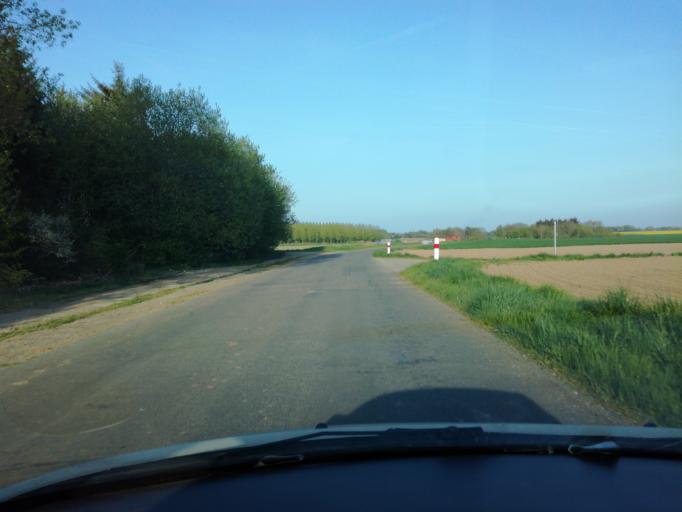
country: FR
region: Picardie
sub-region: Departement de la Somme
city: Poix-de-Picardie
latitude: 49.8181
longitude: 1.9745
